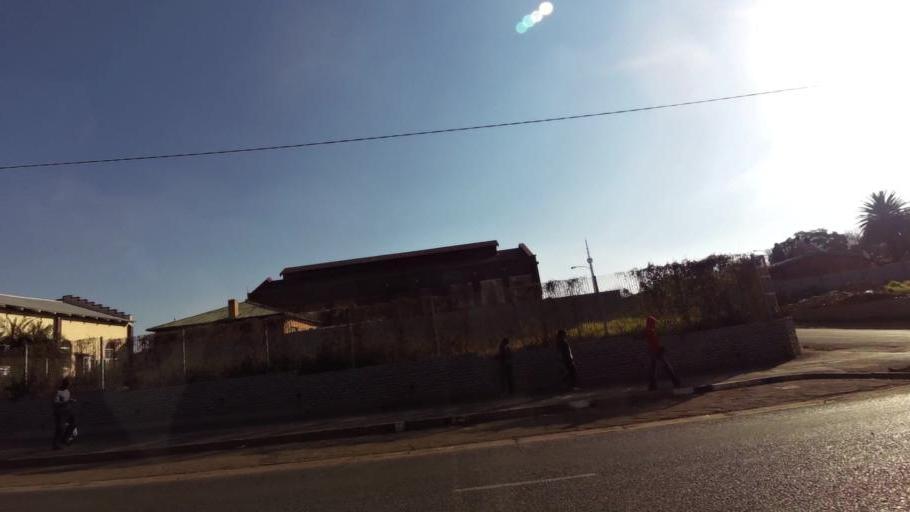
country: ZA
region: Gauteng
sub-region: City of Johannesburg Metropolitan Municipality
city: Johannesburg
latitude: -26.1947
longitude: 28.0205
